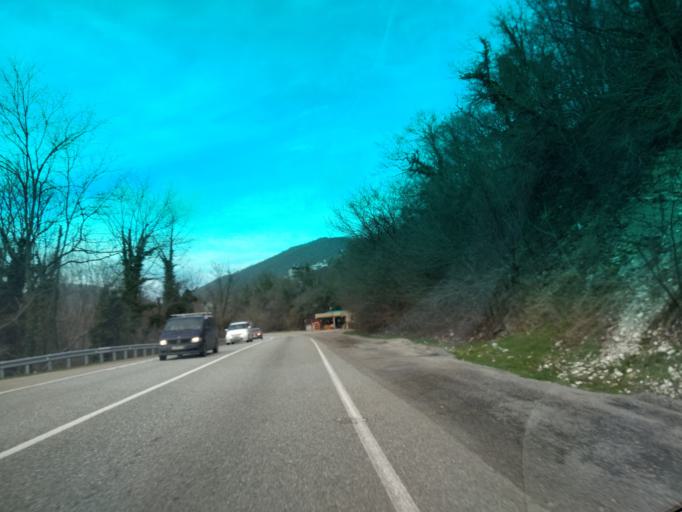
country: RU
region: Krasnodarskiy
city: Shepsi
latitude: 44.0727
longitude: 39.1355
